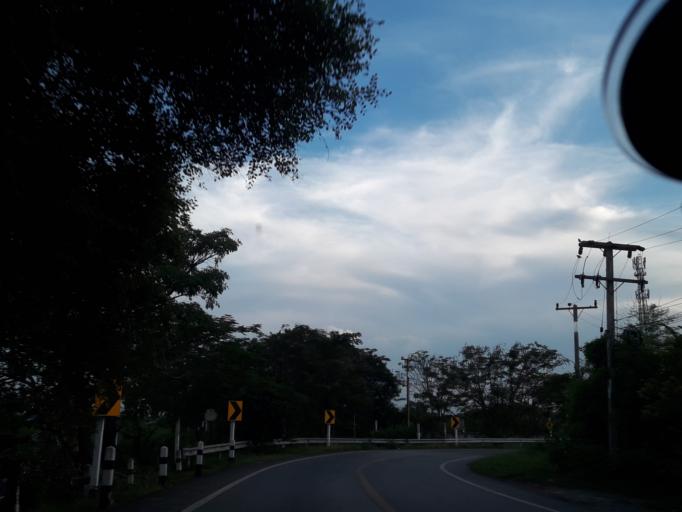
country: TH
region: Sara Buri
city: Nong Khae
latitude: 14.2765
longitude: 100.8912
